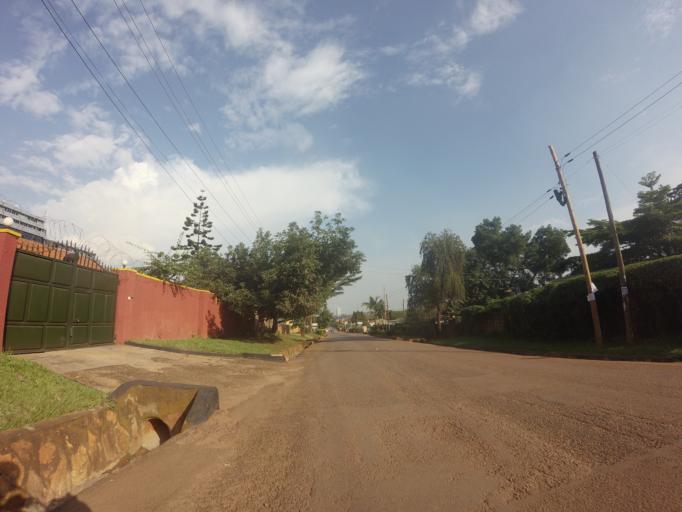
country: UG
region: Central Region
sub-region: Wakiso District
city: Kireka
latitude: 0.3532
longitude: 32.6133
